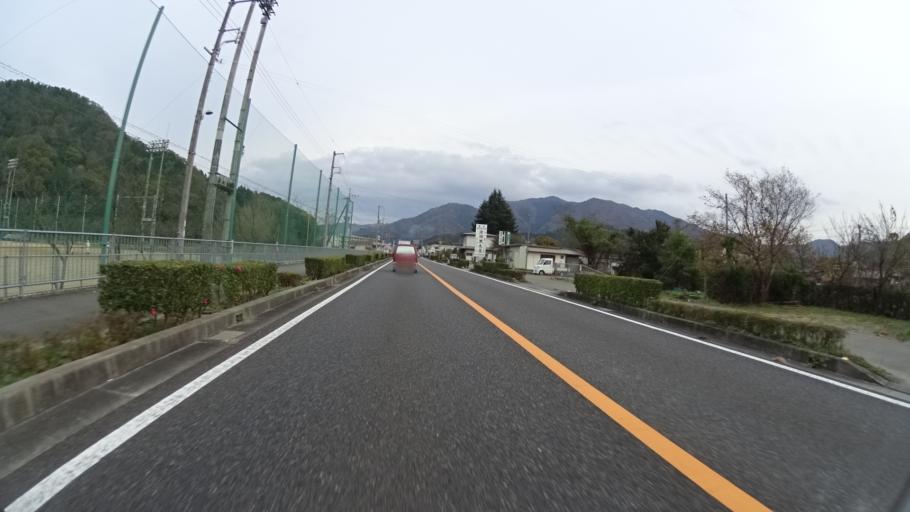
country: JP
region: Hyogo
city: Sasayama
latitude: 35.0696
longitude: 135.2811
